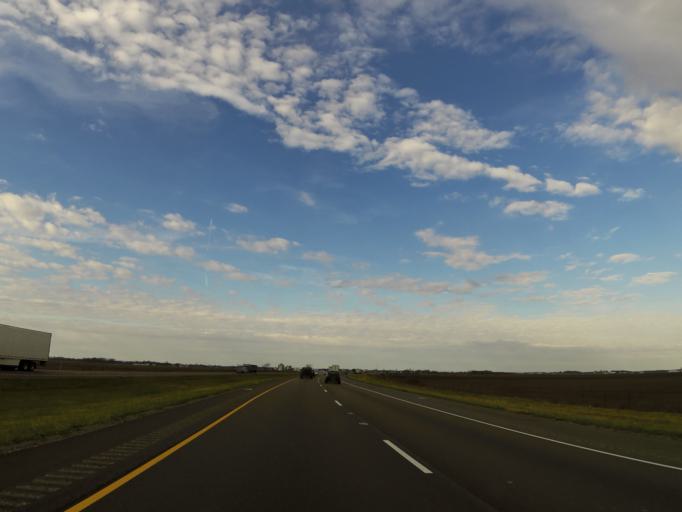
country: US
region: Illinois
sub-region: Washington County
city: Okawville
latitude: 38.4281
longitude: -89.4825
